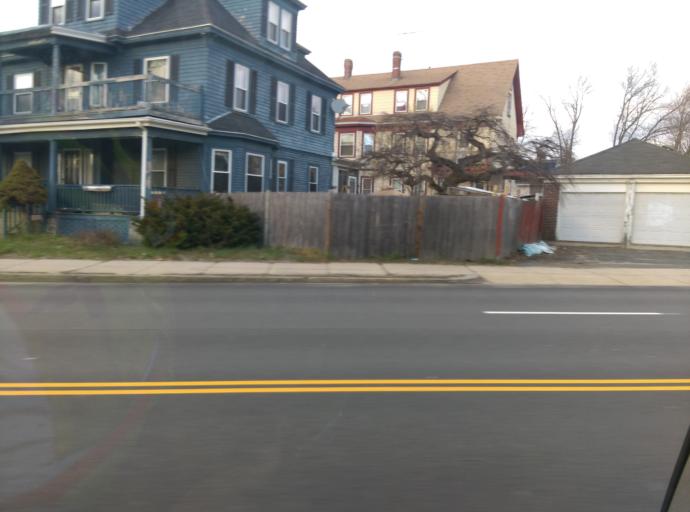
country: US
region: Massachusetts
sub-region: Essex County
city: Lawrence
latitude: 42.6933
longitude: -71.1550
